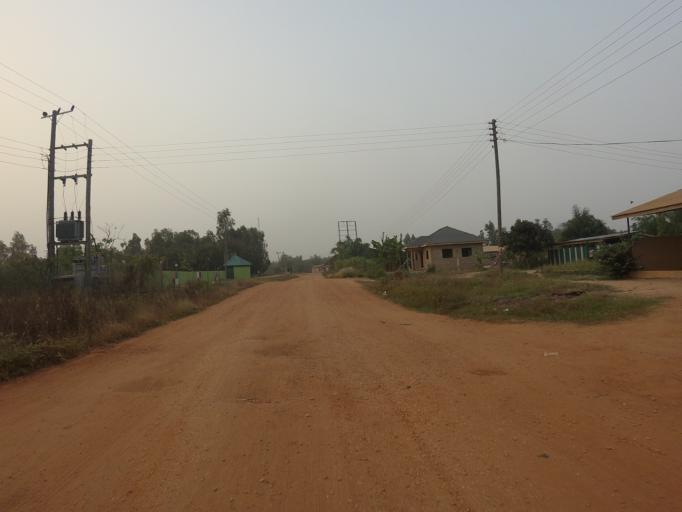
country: GH
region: Volta
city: Anloga
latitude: 5.9888
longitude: 0.5978
